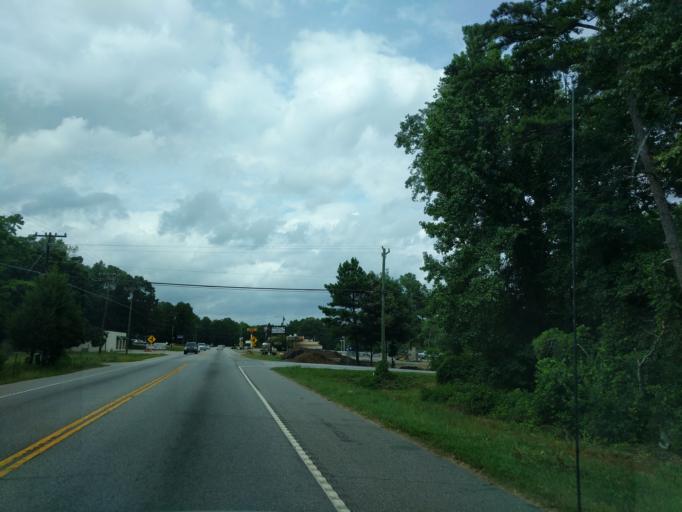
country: US
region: South Carolina
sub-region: Anderson County
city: Anderson
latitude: 34.5190
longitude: -82.5951
